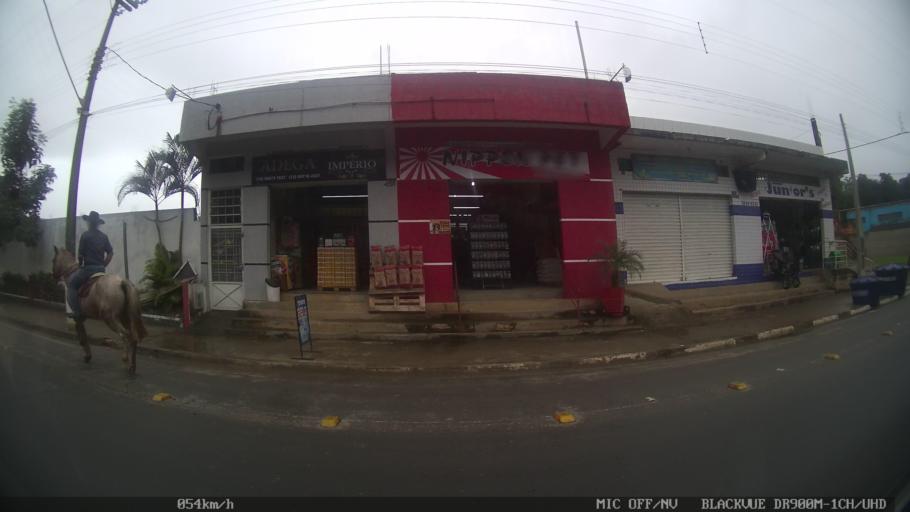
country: BR
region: Sao Paulo
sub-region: Juquia
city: Juquia
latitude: -24.3204
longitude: -47.6389
